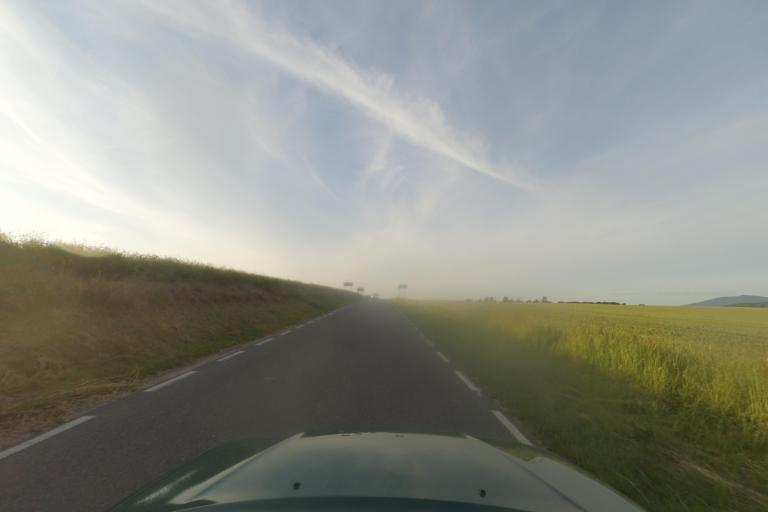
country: PL
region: Lower Silesian Voivodeship
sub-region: Powiat swidnicki
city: Swidnica
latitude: 50.8037
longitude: 16.5372
